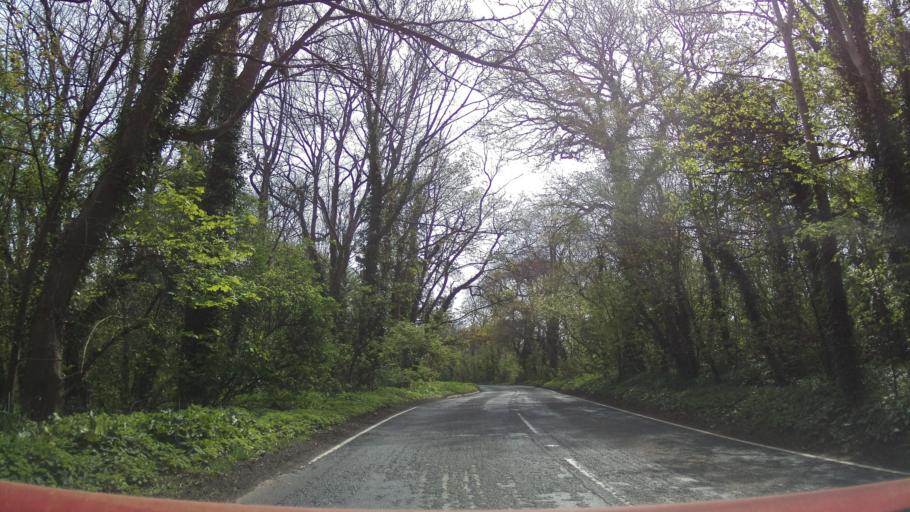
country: GB
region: England
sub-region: Somerset
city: Street
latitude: 51.1097
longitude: -2.7514
